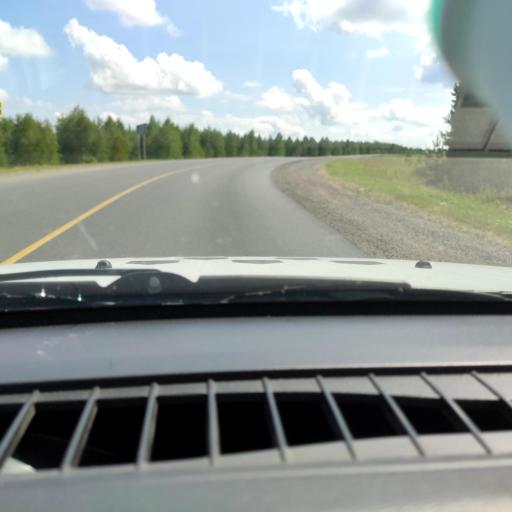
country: RU
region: Bashkortostan
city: Verkhniye Kigi
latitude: 55.3176
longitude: 58.7286
